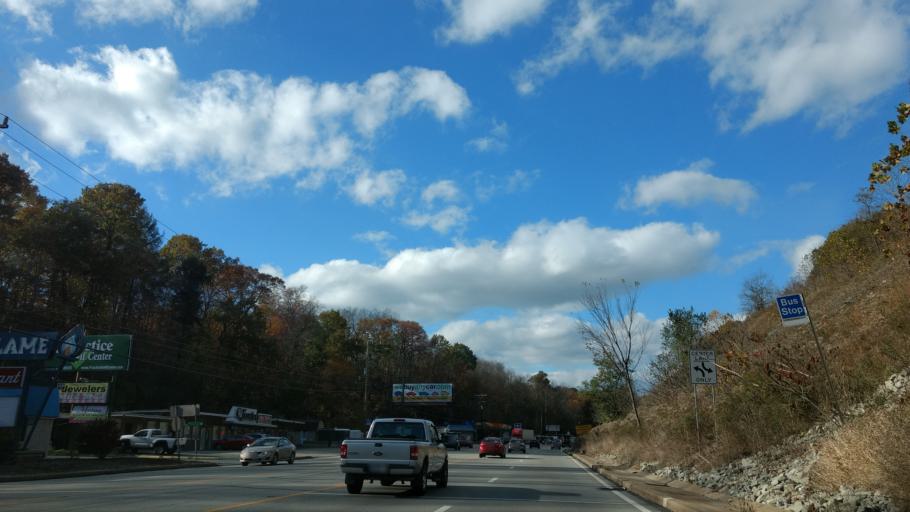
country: US
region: Pennsylvania
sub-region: Allegheny County
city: Jefferson Hills
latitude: 40.3047
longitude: -79.9334
